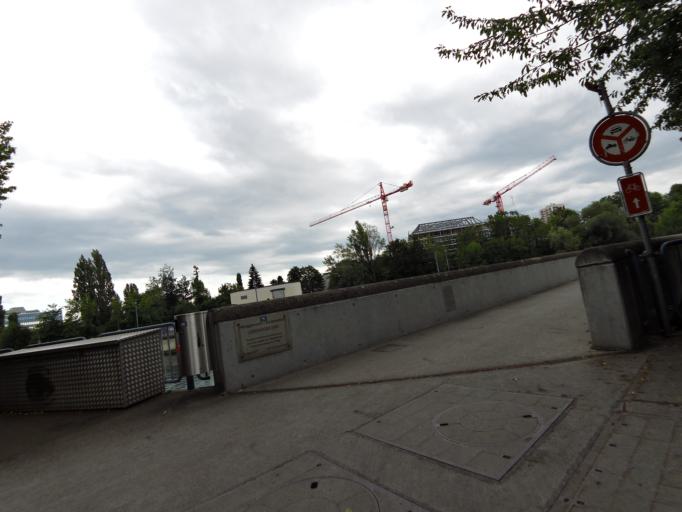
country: CH
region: Zurich
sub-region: Bezirk Zuerich
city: Zuerich (Kreis 10) / Hoengg
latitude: 47.3997
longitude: 8.4930
